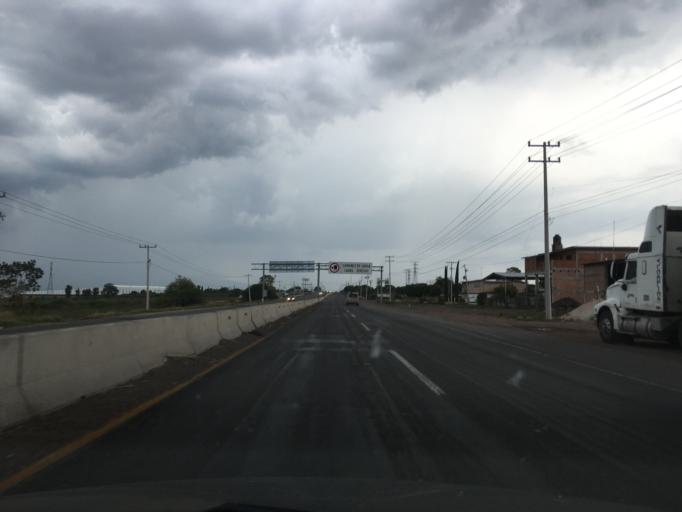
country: MX
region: Guanajuato
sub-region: Celaya
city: El Sauz (El Sauz de Villasenor)
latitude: 20.3798
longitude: -100.7944
